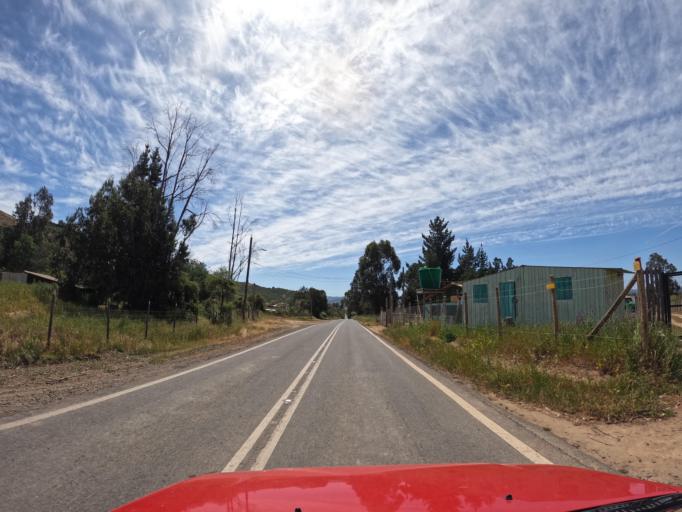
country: CL
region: Maule
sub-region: Provincia de Talca
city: Talca
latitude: -35.0510
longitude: -71.7495
